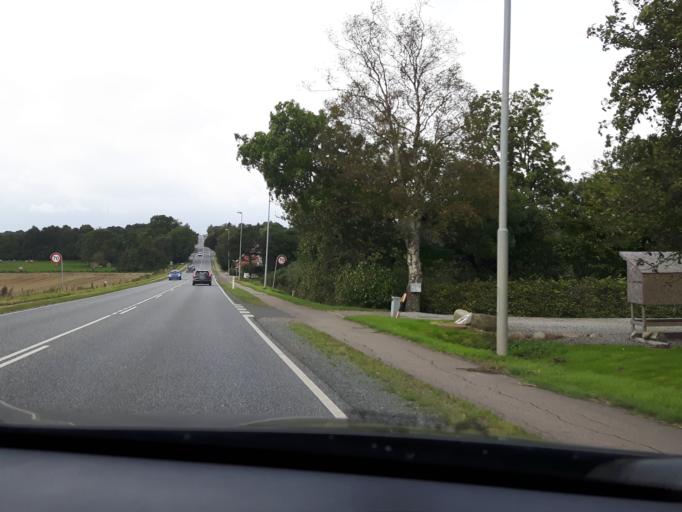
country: DK
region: North Denmark
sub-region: Jammerbugt Kommune
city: Brovst
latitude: 57.0952
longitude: 9.4841
